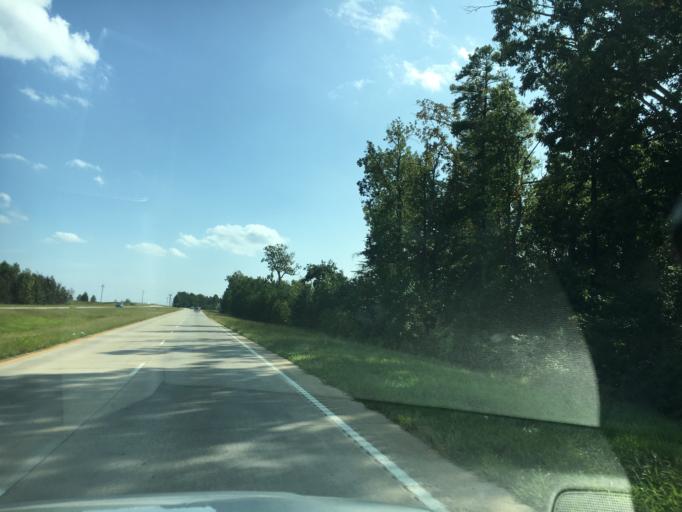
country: US
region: South Carolina
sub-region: Greenville County
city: Greer
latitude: 34.9071
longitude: -82.2192
